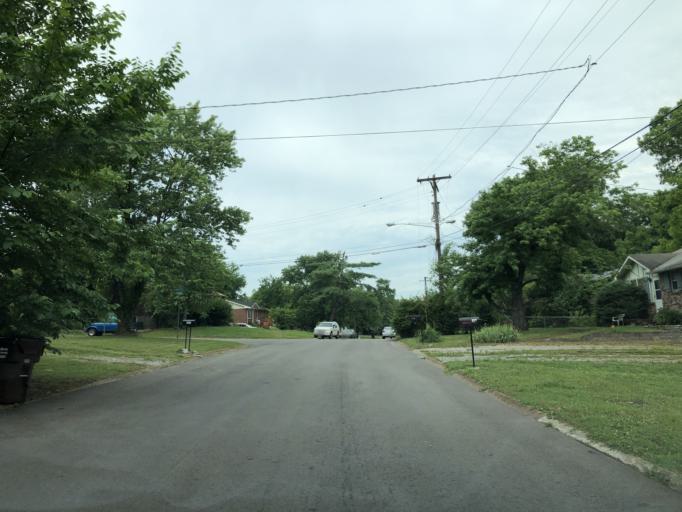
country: US
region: Tennessee
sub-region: Davidson County
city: Goodlettsville
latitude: 36.2855
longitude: -86.6996
